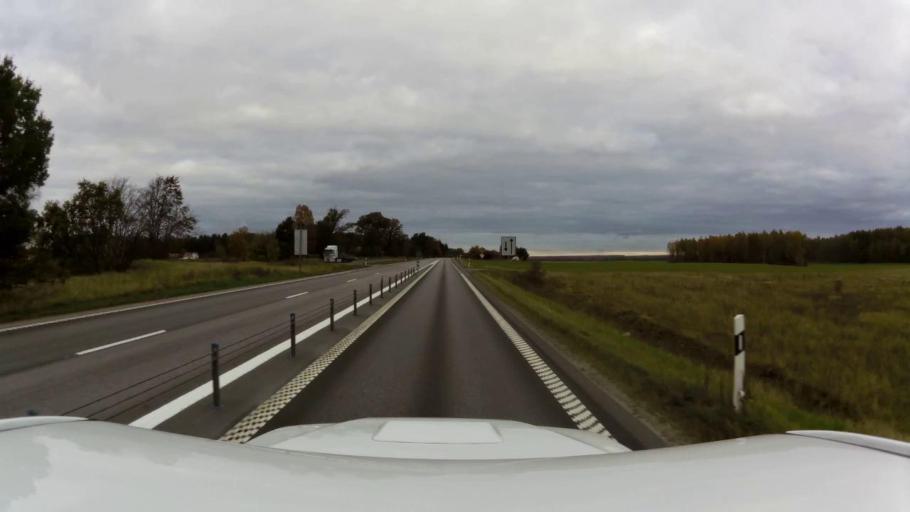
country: SE
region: OEstergoetland
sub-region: Linkopings Kommun
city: Ljungsbro
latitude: 58.4983
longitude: 15.4590
